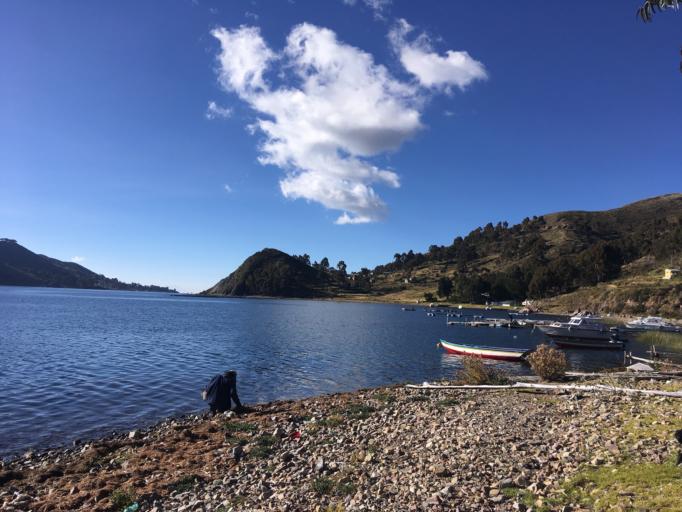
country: BO
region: La Paz
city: San Pedro
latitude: -16.2073
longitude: -68.8748
